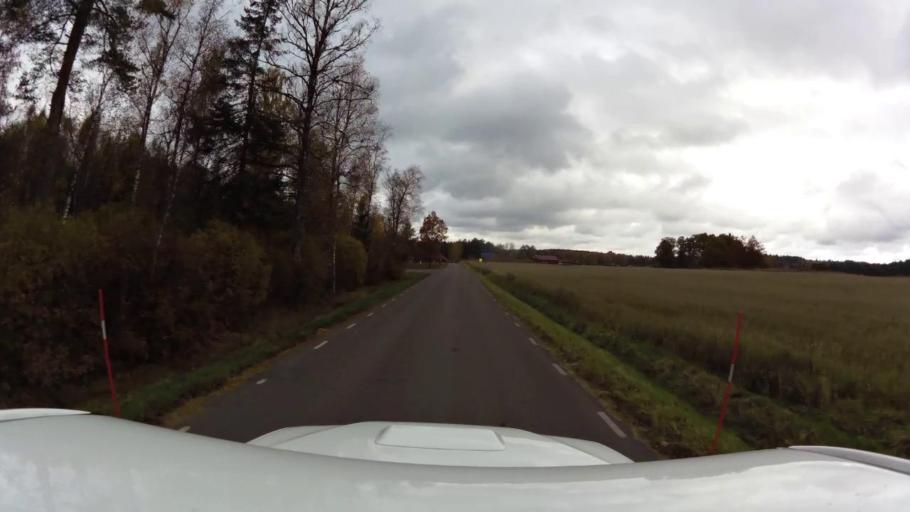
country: SE
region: OEstergoetland
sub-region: Motala Kommun
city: Borensberg
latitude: 58.5647
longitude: 15.3895
